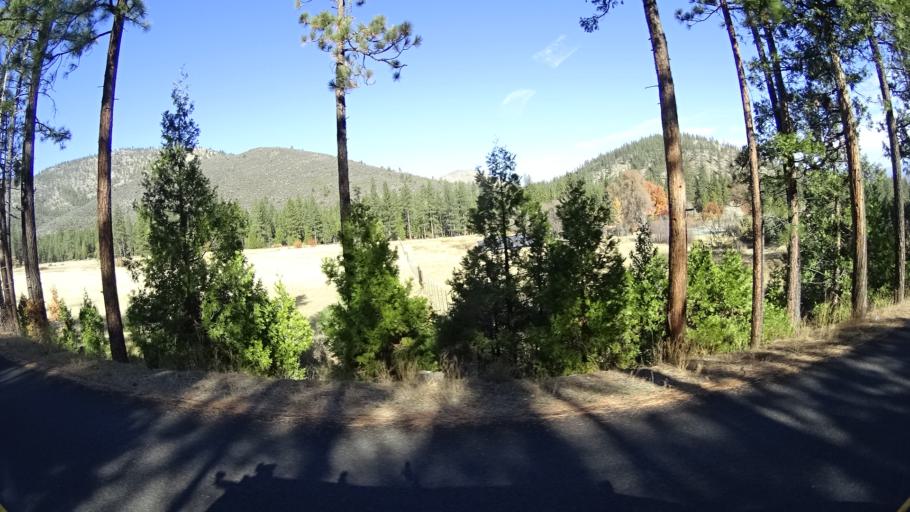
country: US
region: California
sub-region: Siskiyou County
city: Weed
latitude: 41.4325
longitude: -122.4845
